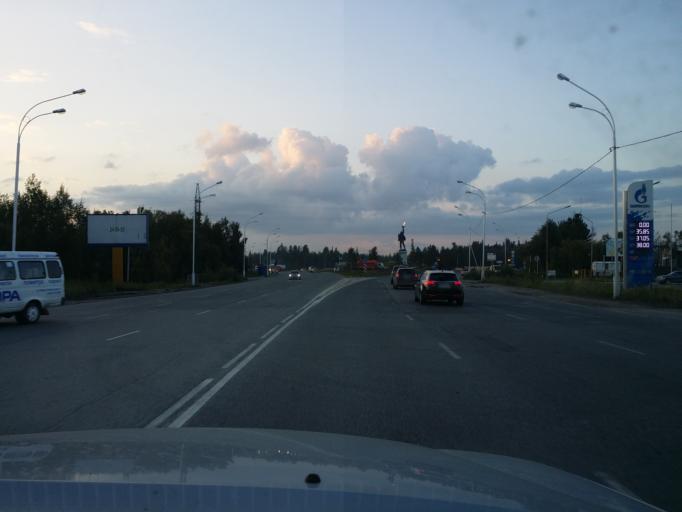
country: RU
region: Khanty-Mansiyskiy Avtonomnyy Okrug
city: Nizhnevartovsk
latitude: 60.9666
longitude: 76.5308
